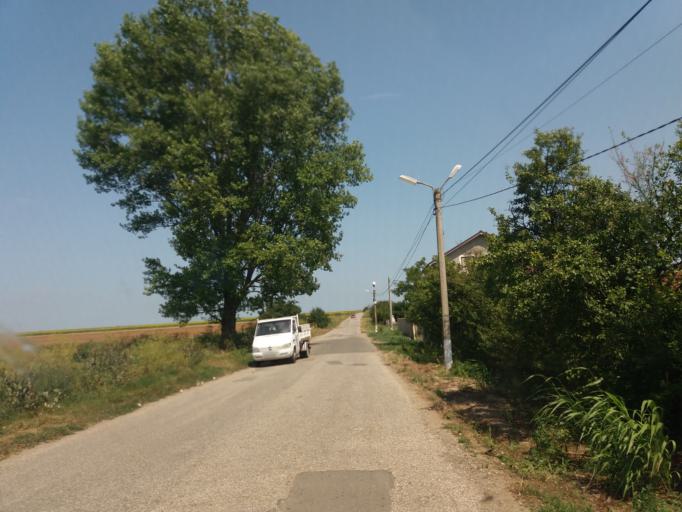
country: RO
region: Constanta
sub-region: Comuna Corbu
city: Corbu
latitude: 44.4240
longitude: 28.6613
